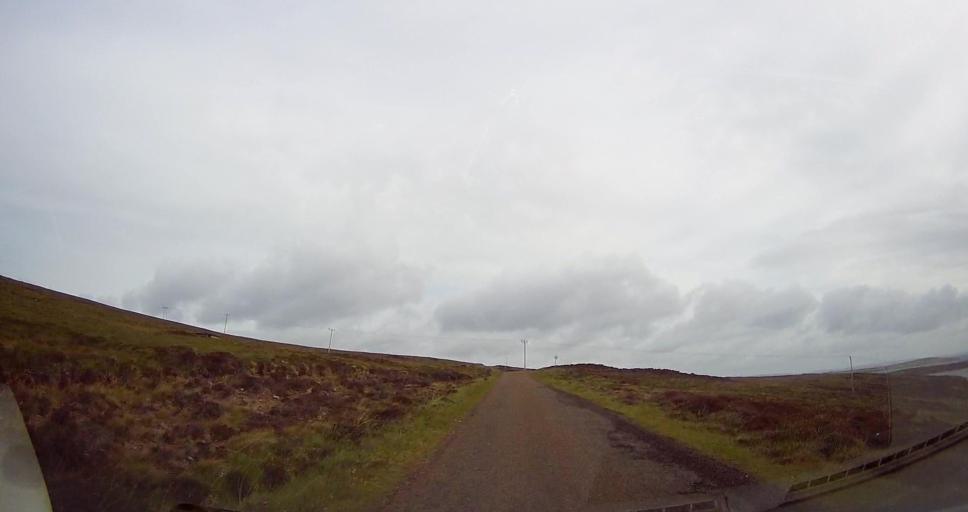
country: GB
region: Scotland
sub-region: Orkney Islands
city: Stromness
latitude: 58.8615
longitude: -3.2234
